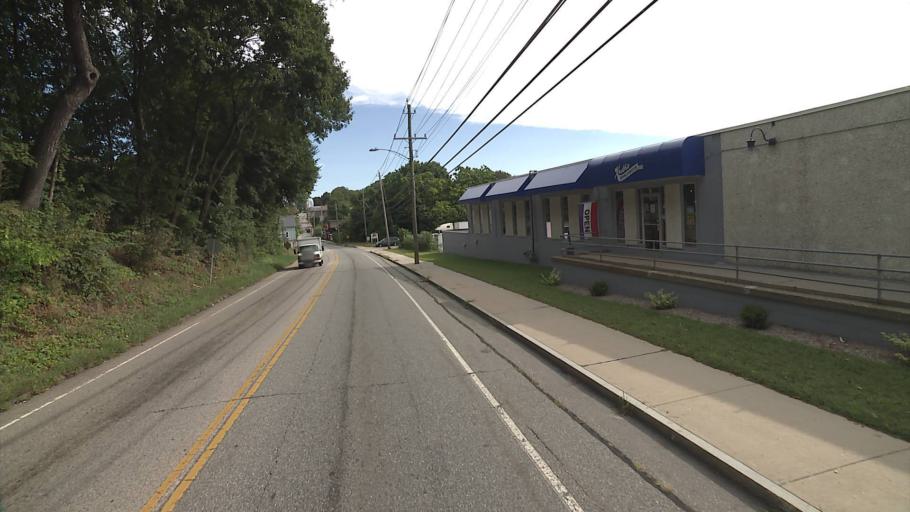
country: US
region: Connecticut
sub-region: New London County
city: Norwich
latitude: 41.5086
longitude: -72.0858
